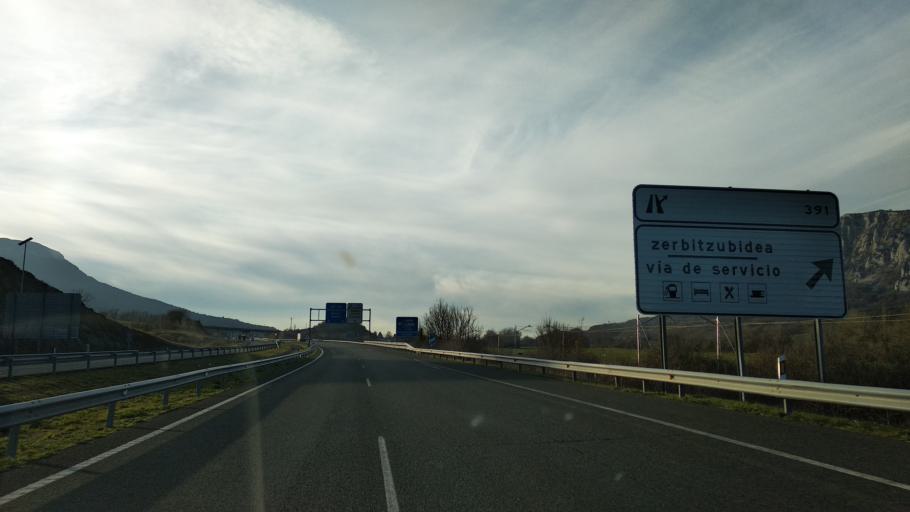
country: ES
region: Navarre
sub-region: Provincia de Navarra
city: Ziordia
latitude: 42.8662
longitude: -2.2430
